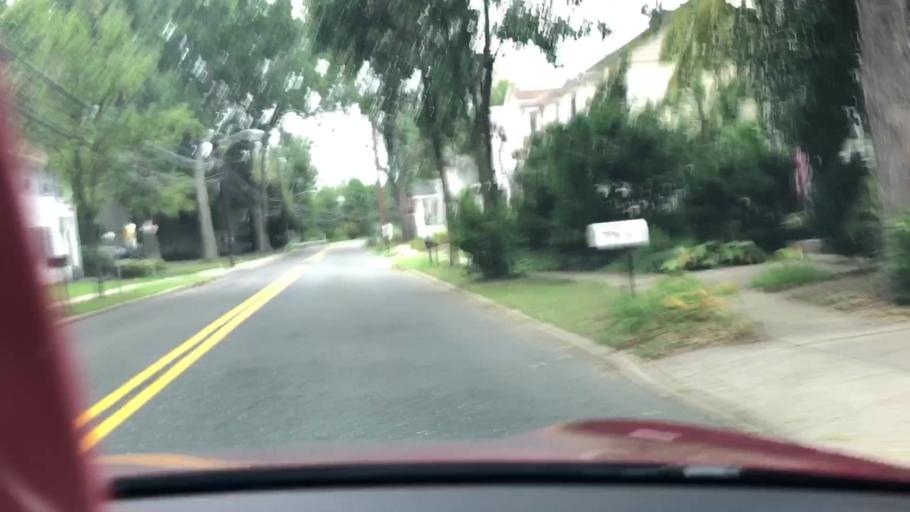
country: US
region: New Jersey
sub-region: Monmouth County
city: Allentown
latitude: 40.1805
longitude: -74.5882
